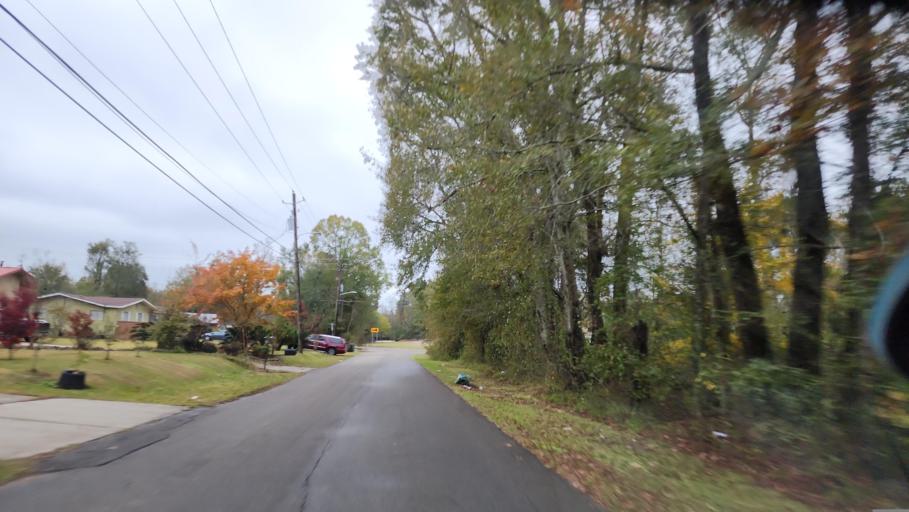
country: US
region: Mississippi
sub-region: Forrest County
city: Hattiesburg
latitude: 31.3039
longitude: -89.2994
